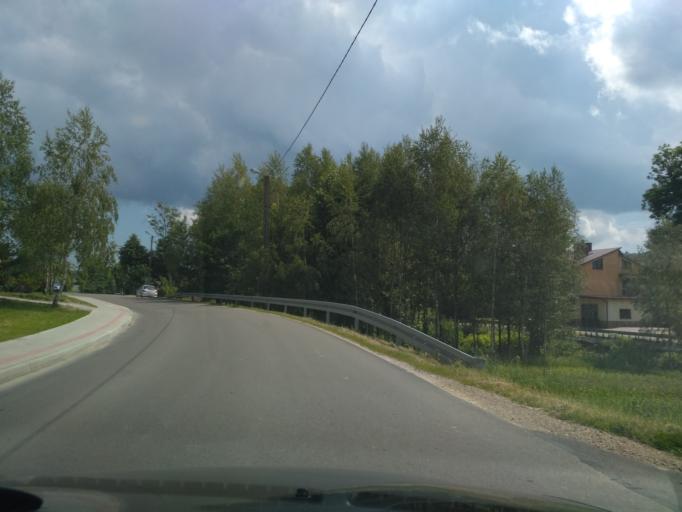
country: PL
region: Subcarpathian Voivodeship
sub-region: Powiat rzeszowski
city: Blazowa
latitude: 49.8753
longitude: 22.0760
